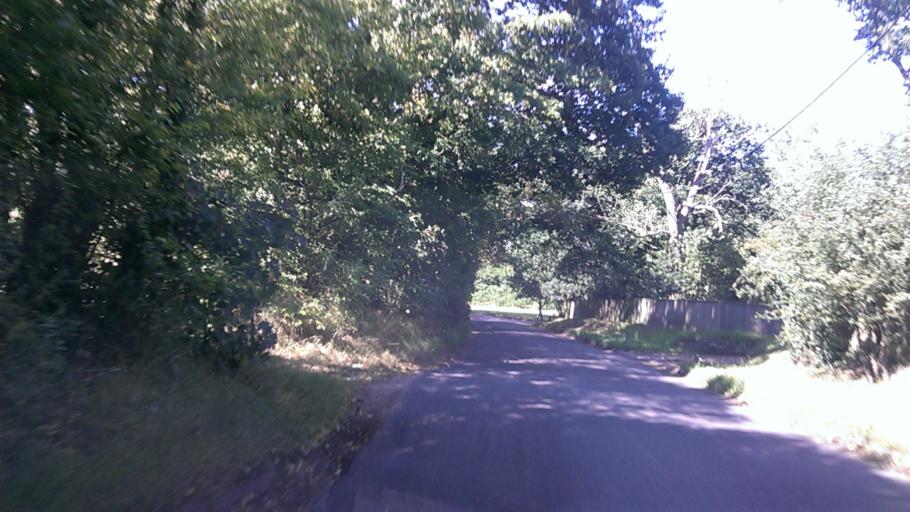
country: GB
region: England
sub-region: Essex
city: Layer de la Haye
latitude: 51.8595
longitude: 0.8833
